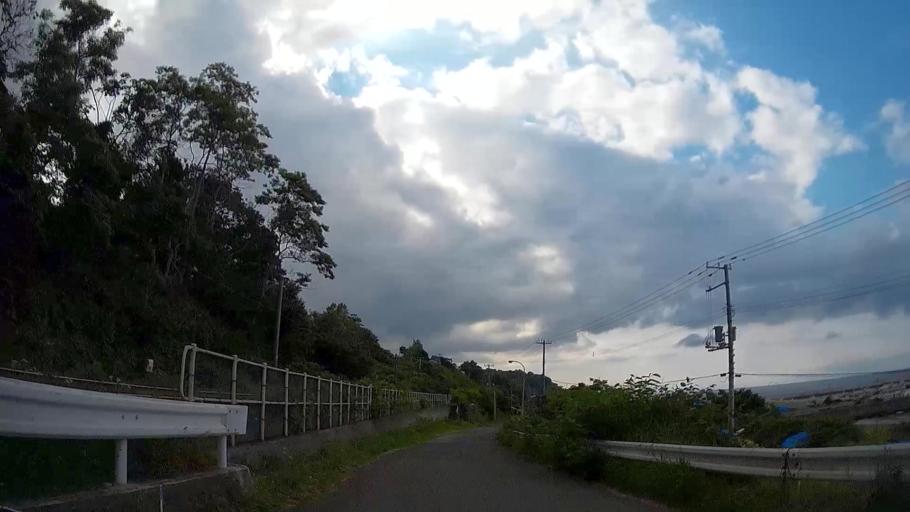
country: JP
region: Hokkaido
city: Nanae
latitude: 42.1140
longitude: 140.5461
